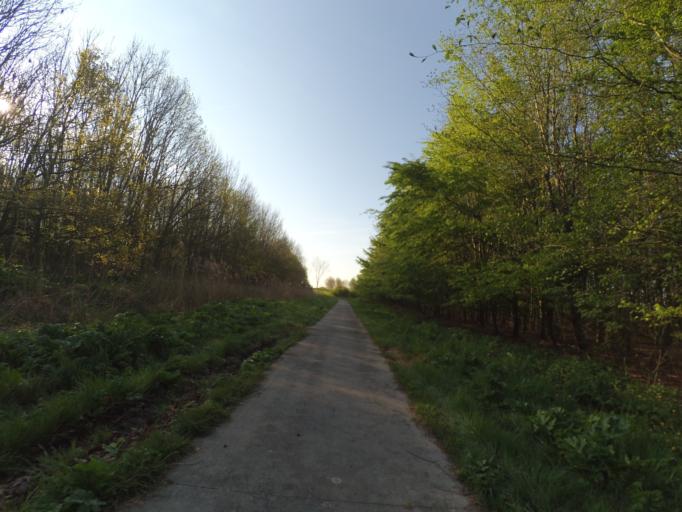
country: NL
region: Flevoland
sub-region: Gemeente Almere
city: Almere Stad
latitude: 52.3951
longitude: 5.3303
